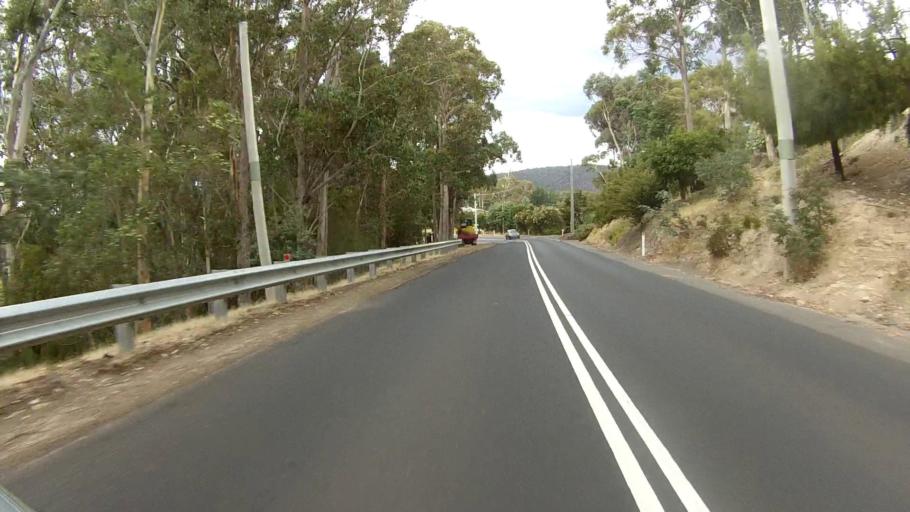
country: AU
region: Tasmania
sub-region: Hobart
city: Dynnyrne
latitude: -42.9051
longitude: 147.2787
